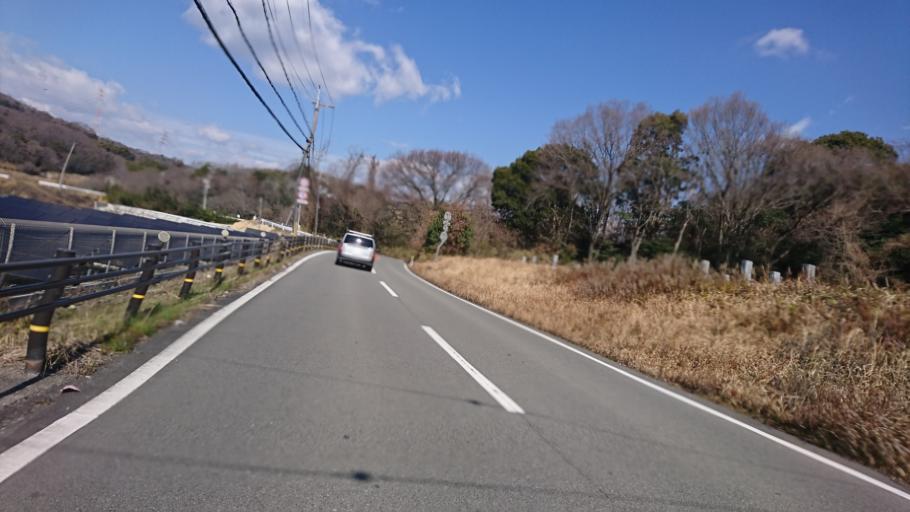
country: JP
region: Hyogo
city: Kakogawacho-honmachi
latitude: 34.8286
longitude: 134.8220
